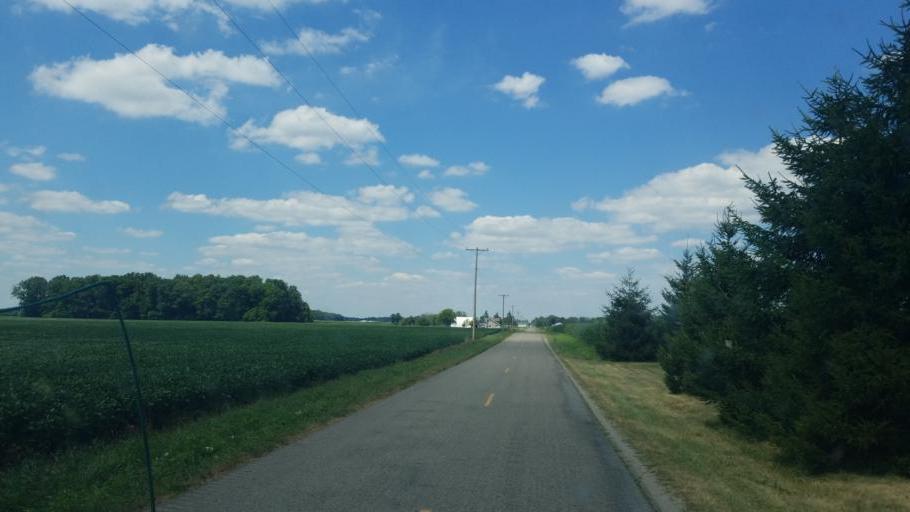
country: US
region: Ohio
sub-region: Defiance County
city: Hicksville
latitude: 41.2982
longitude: -84.7281
